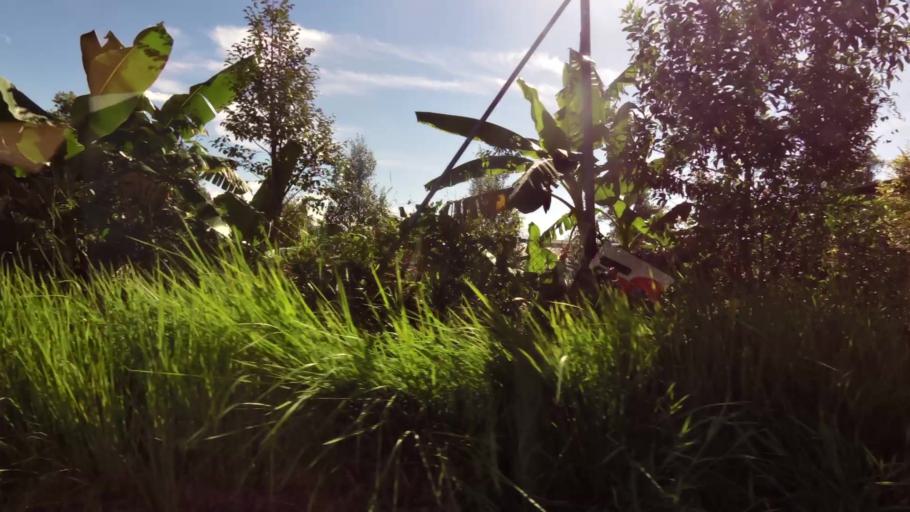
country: BN
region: Brunei and Muara
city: Bandar Seri Begawan
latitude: 4.9659
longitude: 114.9347
